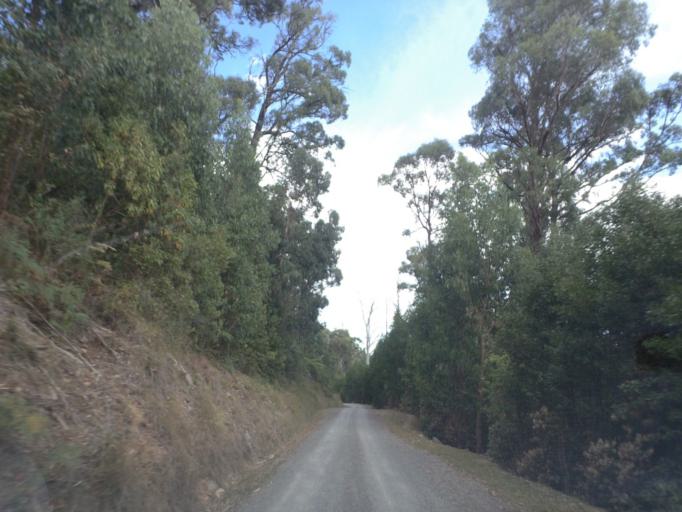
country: AU
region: Victoria
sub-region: Murrindindi
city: Alexandra
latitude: -37.4161
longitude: 145.7592
